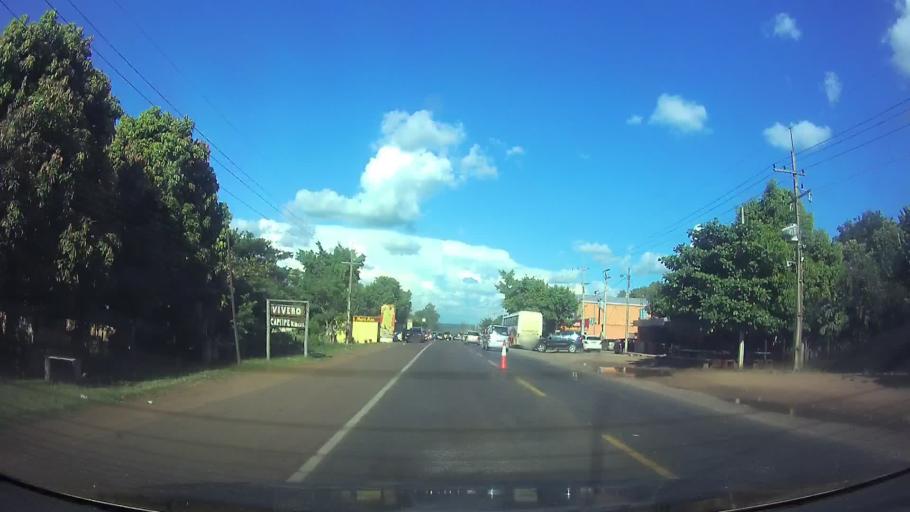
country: PY
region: Cordillera
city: Eusebio Ayala
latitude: -25.3817
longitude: -57.0021
